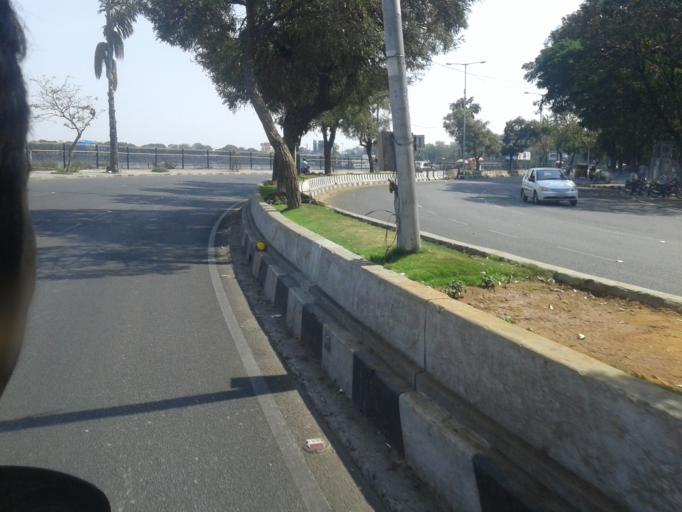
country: IN
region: Telangana
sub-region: Hyderabad
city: Hyderabad
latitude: 17.4140
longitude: 78.4706
